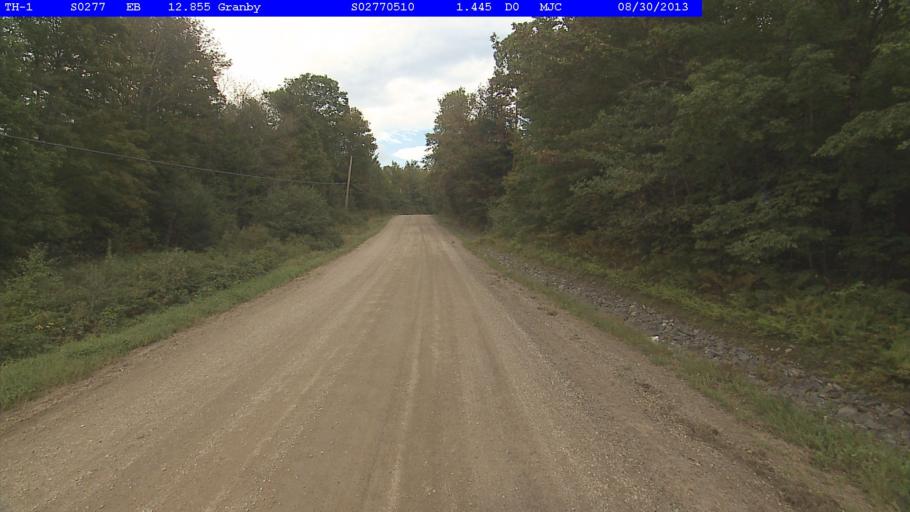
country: US
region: Vermont
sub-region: Essex County
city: Guildhall
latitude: 44.5744
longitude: -71.7362
